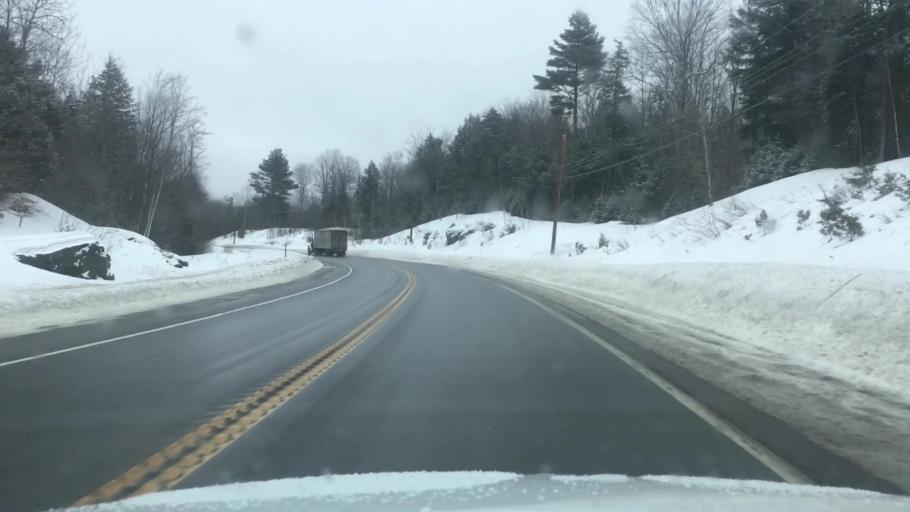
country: US
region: Maine
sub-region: Oxford County
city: Peru
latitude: 44.5535
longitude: -70.3831
